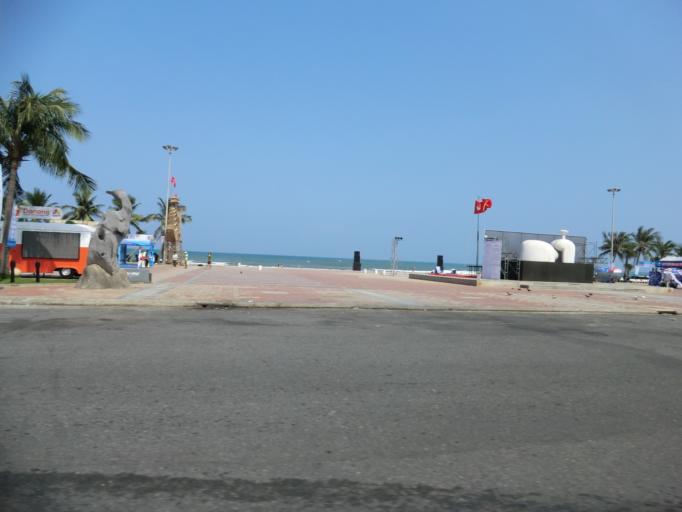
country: VN
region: Da Nang
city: Son Tra
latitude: 16.0705
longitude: 108.2453
